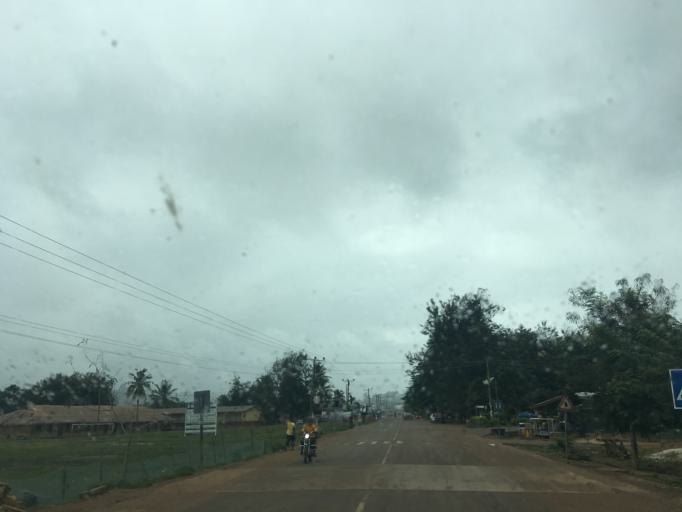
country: GH
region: Western
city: Wassa-Akropong
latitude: 5.8047
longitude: -2.4321
